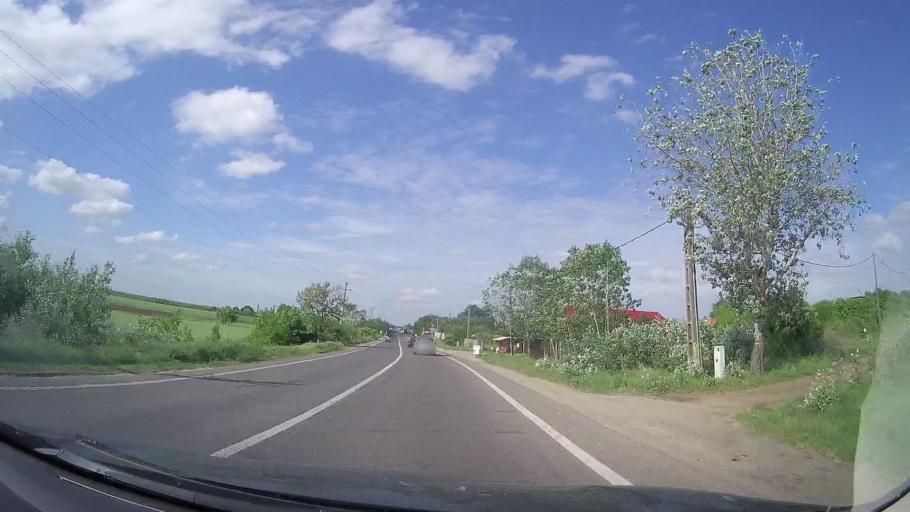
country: RO
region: Giurgiu
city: Iepuresti
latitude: 44.2934
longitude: 25.8736
